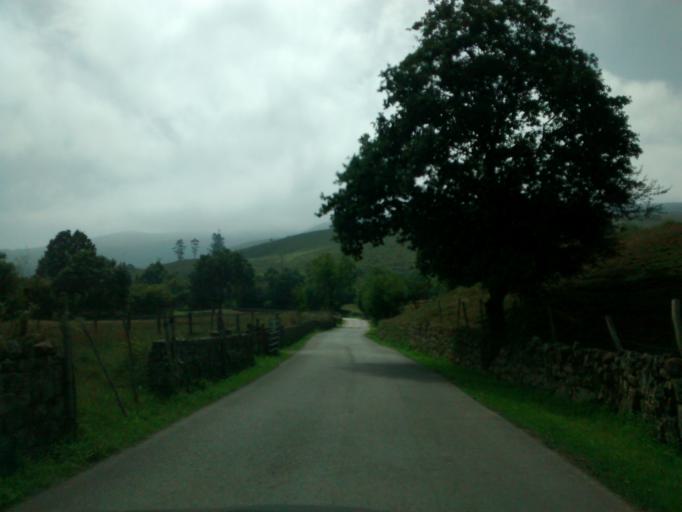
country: ES
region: Cantabria
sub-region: Provincia de Cantabria
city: Ruente
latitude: 43.2529
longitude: -4.2450
